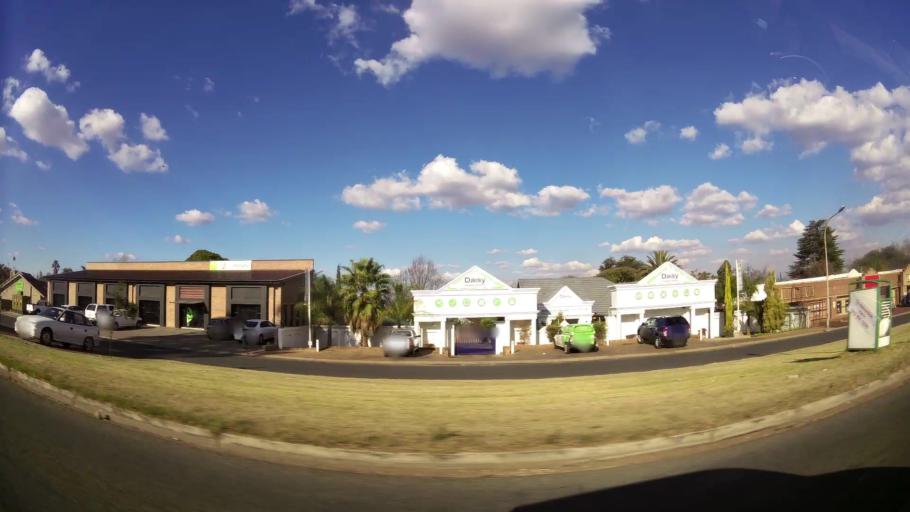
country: ZA
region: Mpumalanga
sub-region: Nkangala District Municipality
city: Witbank
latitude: -25.8809
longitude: 29.2356
